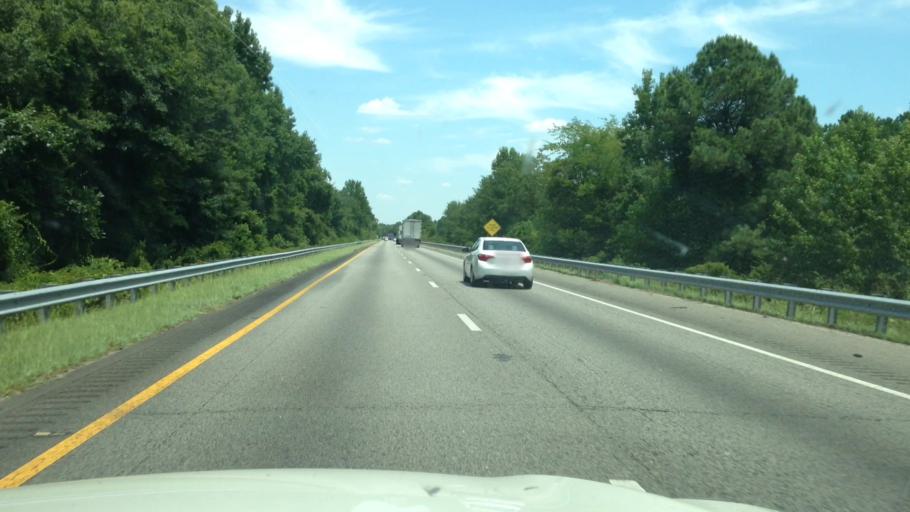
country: US
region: South Carolina
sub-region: Florence County
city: Florence
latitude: 34.2867
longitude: -79.6643
